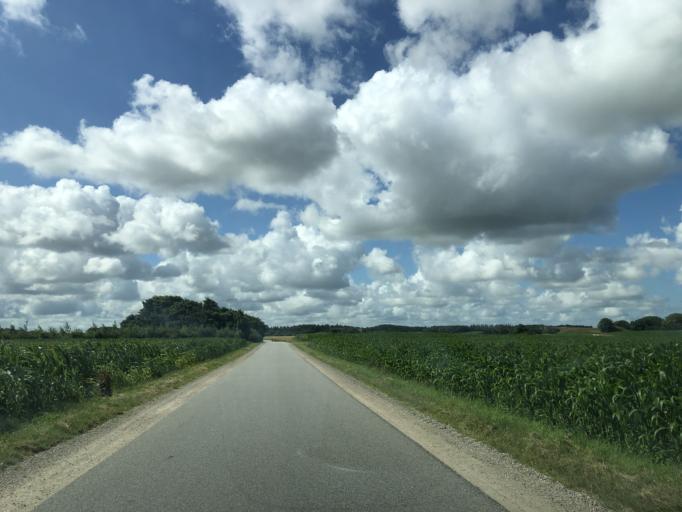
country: DK
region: Central Jutland
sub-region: Struer Kommune
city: Struer
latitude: 56.4447
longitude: 8.5162
